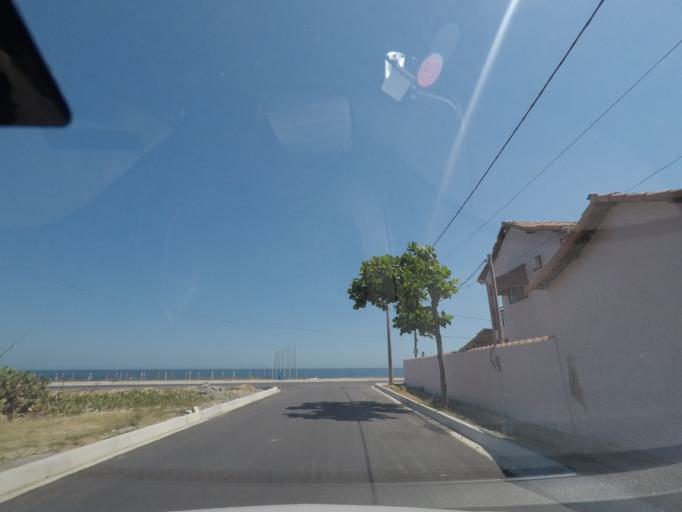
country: BR
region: Rio de Janeiro
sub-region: Marica
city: Marica
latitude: -22.9711
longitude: -42.9046
